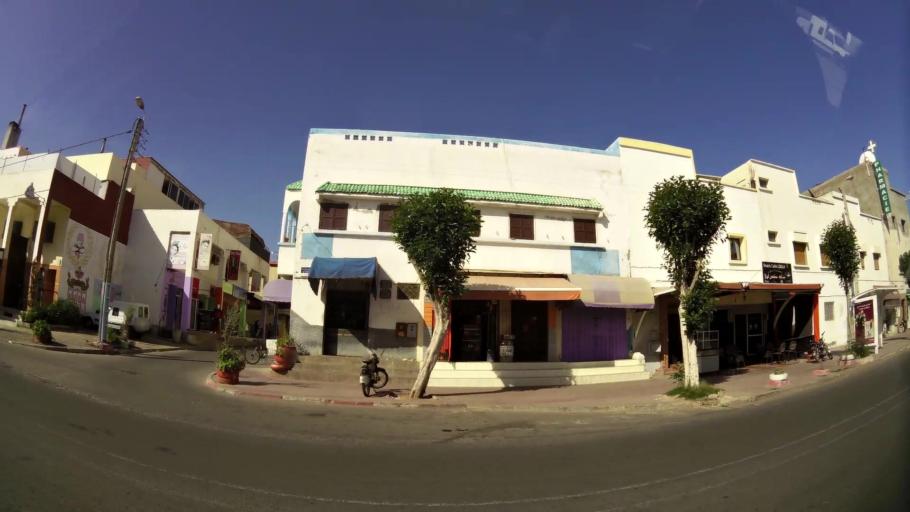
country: MA
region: Oued ed Dahab-Lagouira
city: Dakhla
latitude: 30.4243
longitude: -9.5646
